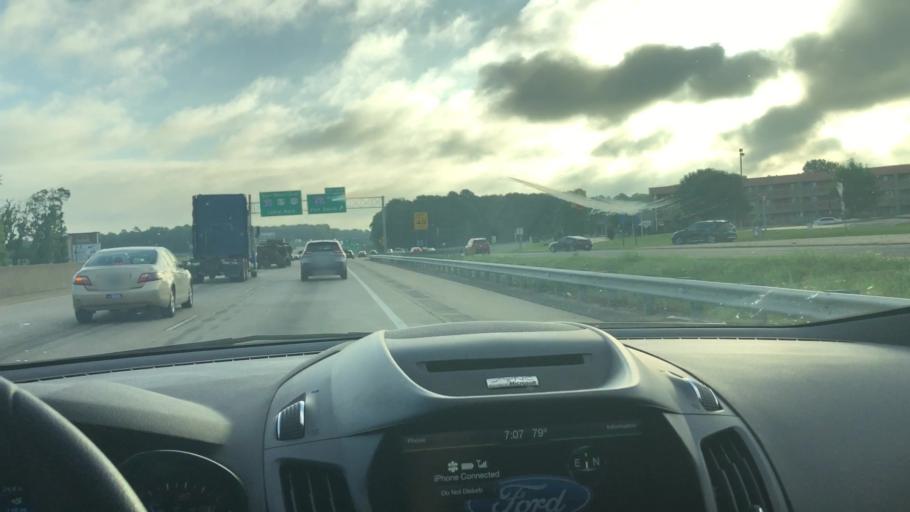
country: US
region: Arkansas
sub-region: Saline County
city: Shannon Hills
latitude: 34.6568
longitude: -92.4084
